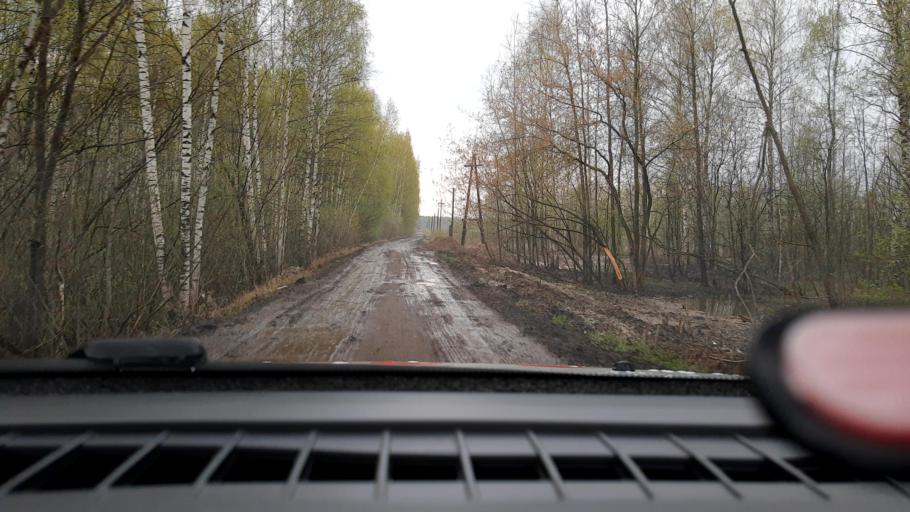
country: RU
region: Nizjnij Novgorod
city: Gorbatovka
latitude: 56.3001
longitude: 43.7701
